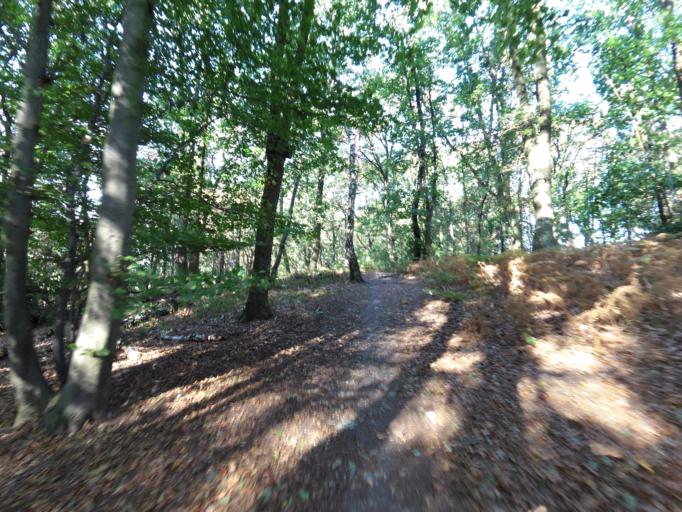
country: NL
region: Limburg
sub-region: Gemeente Kerkrade
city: Kerkrade
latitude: 50.8991
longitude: 6.0394
